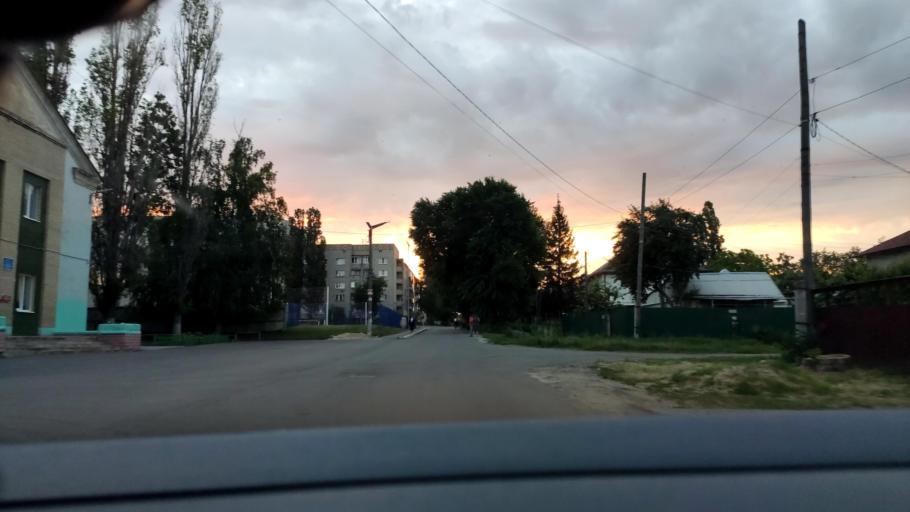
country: RU
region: Voronezj
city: Semiluki
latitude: 51.6941
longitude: 39.0256
